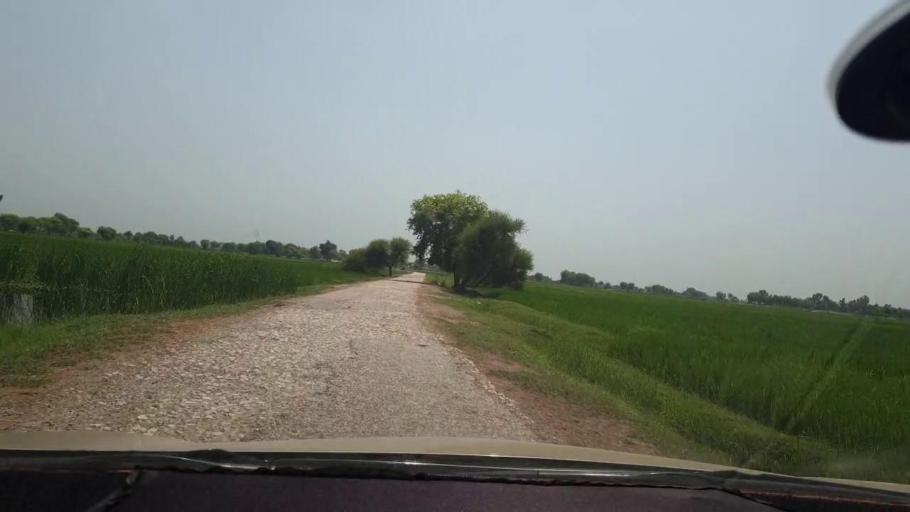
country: PK
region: Sindh
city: Kambar
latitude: 27.6425
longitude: 67.9323
